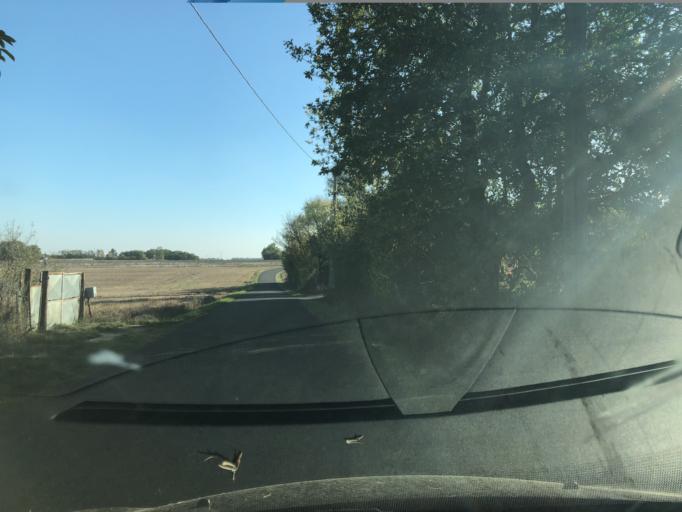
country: FR
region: Centre
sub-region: Departement d'Indre-et-Loire
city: Neuvy-le-Roi
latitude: 47.6646
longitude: 0.6085
